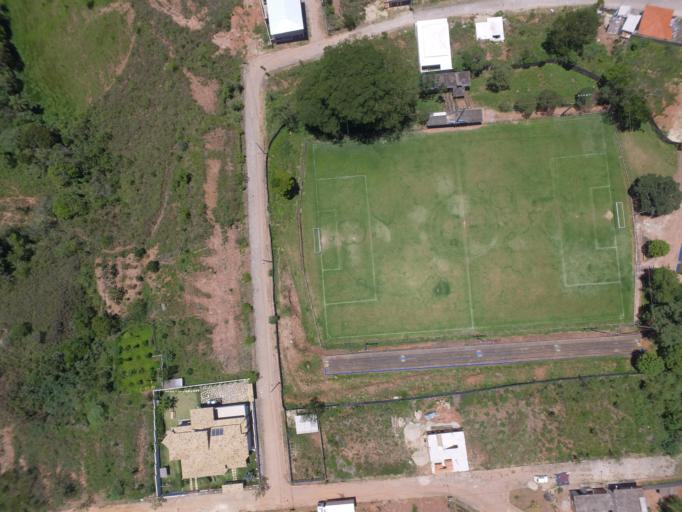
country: BR
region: Minas Gerais
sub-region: Tiradentes
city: Tiradentes
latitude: -21.0641
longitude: -44.0791
